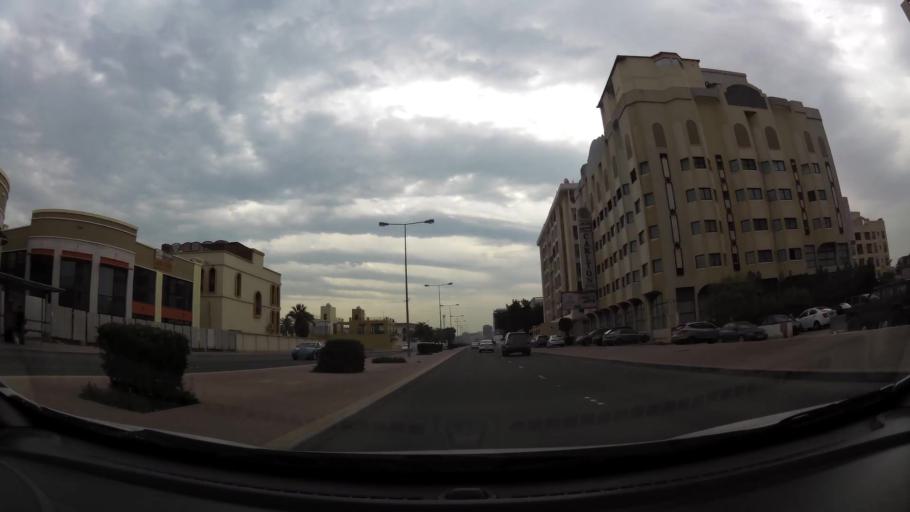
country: BH
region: Manama
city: Manama
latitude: 26.2132
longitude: 50.5907
